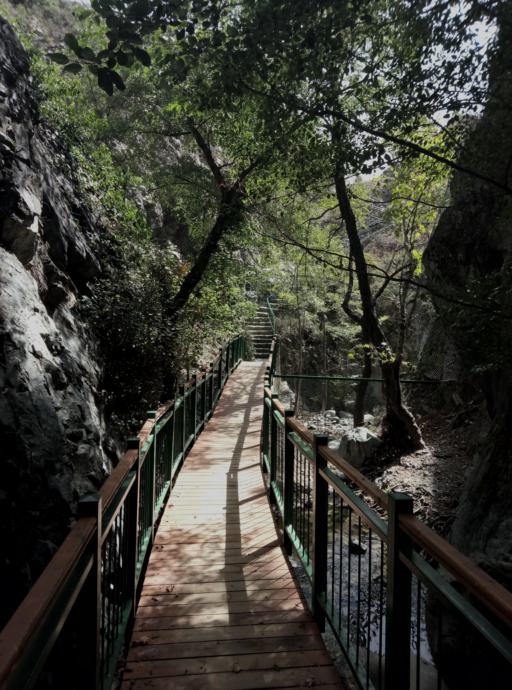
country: CY
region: Limassol
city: Pelendri
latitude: 34.8836
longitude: 32.8657
